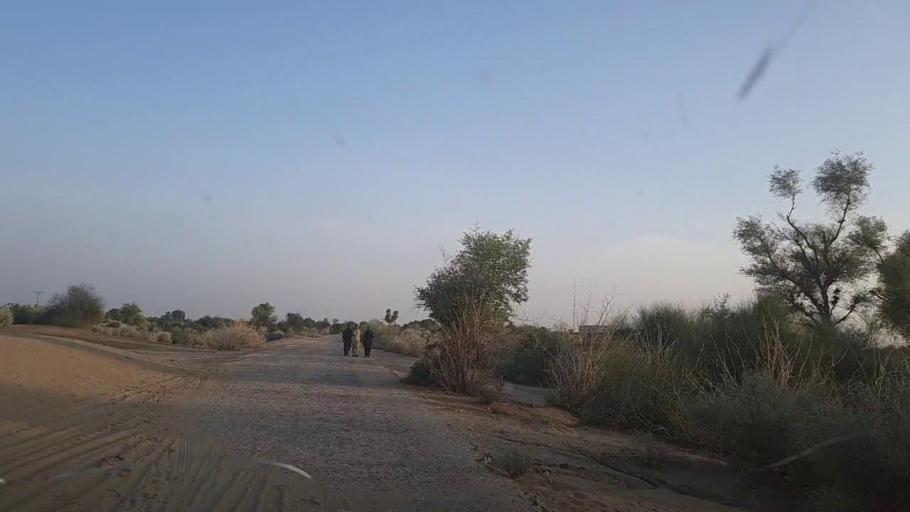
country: PK
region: Sindh
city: Khanpur
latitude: 27.6287
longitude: 69.4446
